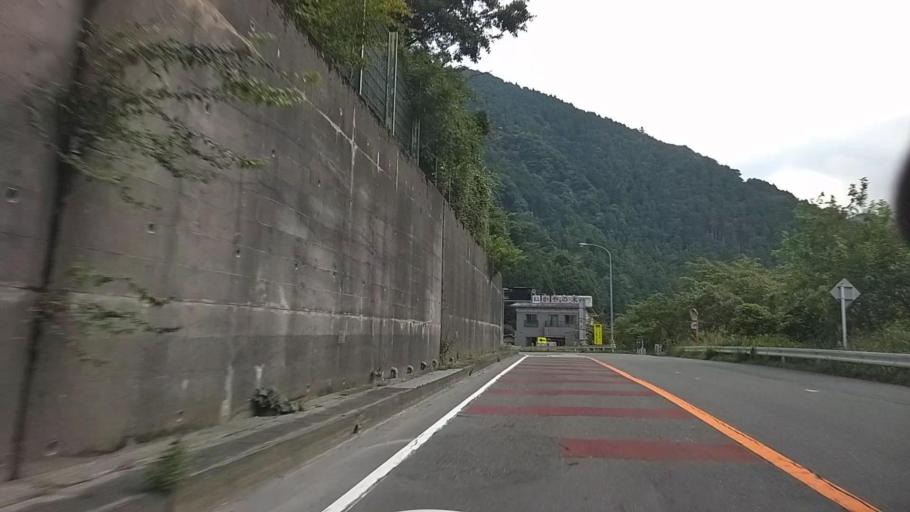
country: JP
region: Shizuoka
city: Fujinomiya
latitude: 35.3269
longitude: 138.4287
